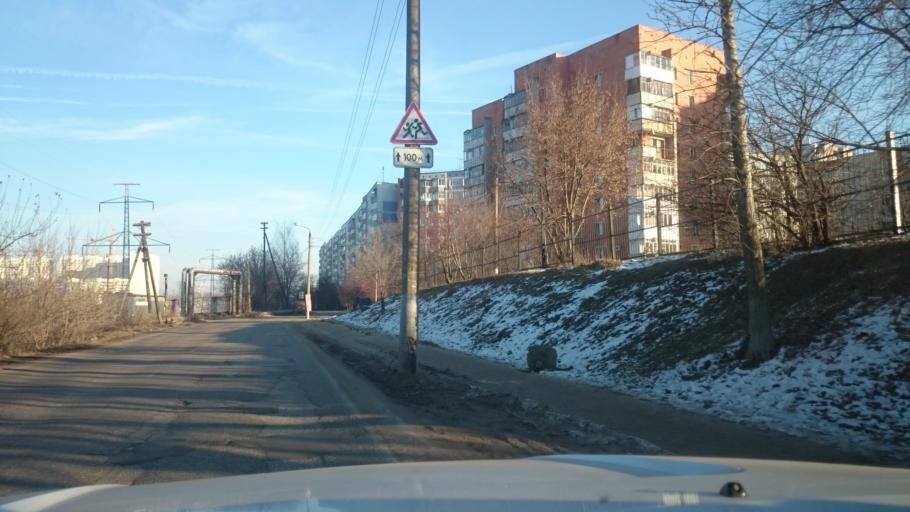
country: RU
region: Tula
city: Tula
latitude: 54.2064
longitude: 37.6811
